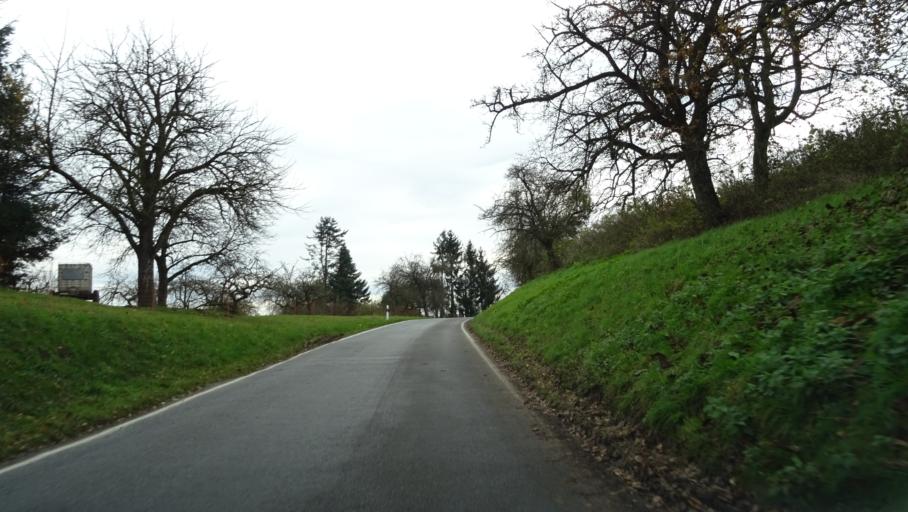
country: DE
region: Baden-Wuerttemberg
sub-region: Karlsruhe Region
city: Neckargerach
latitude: 49.3922
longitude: 9.0979
